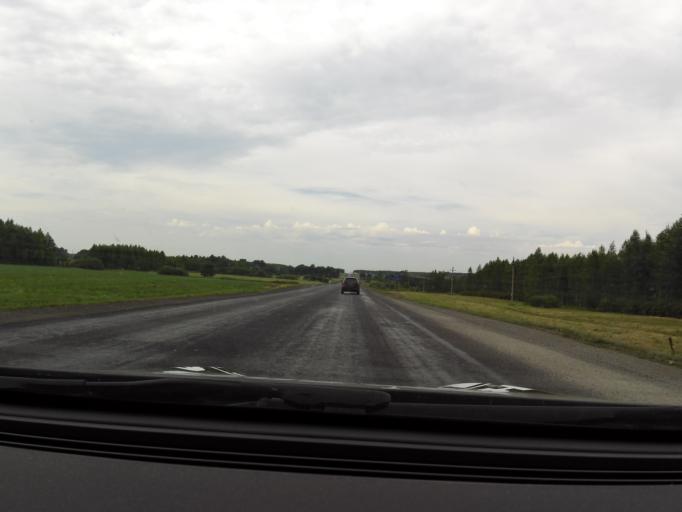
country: RU
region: Bashkortostan
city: Iglino
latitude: 54.7517
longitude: 56.3371
